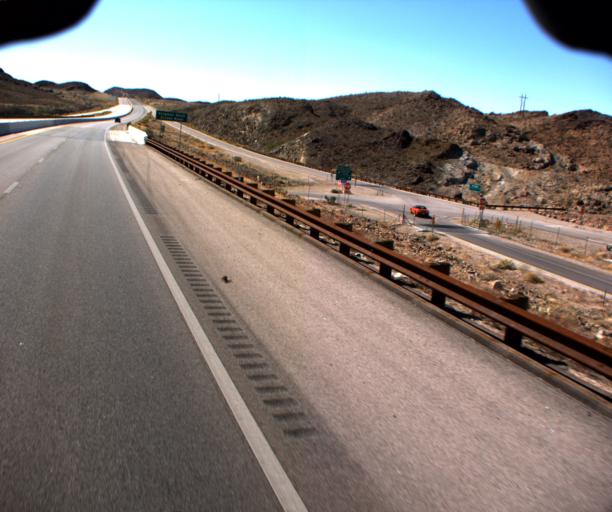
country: US
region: Nevada
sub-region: Clark County
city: Boulder City
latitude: 36.0027
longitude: -114.7229
